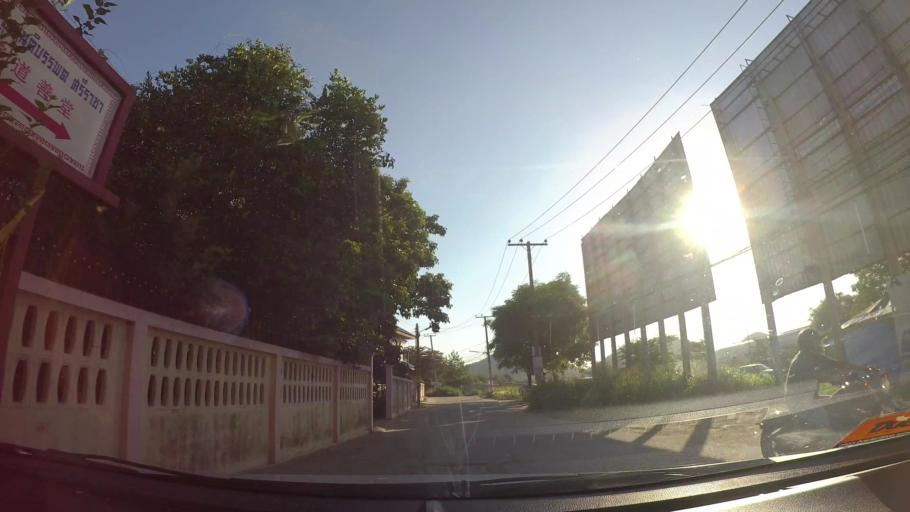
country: TH
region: Chon Buri
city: Si Racha
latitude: 13.1405
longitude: 100.9380
